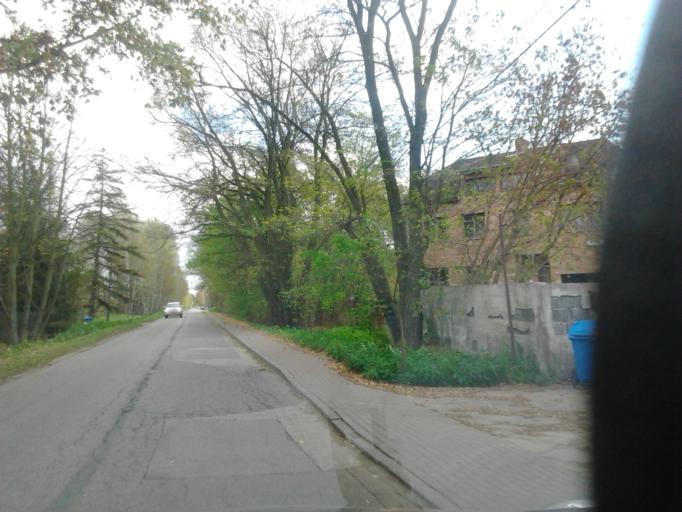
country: PL
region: Masovian Voivodeship
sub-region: Powiat pruszkowski
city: Nadarzyn
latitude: 52.0927
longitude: 20.8174
